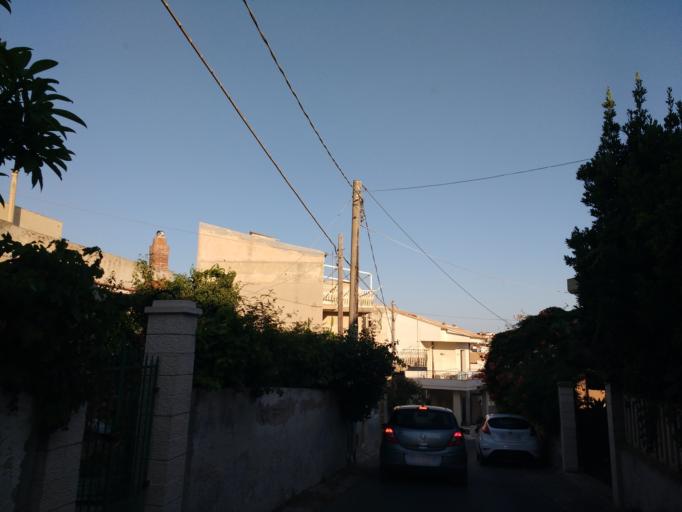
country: IT
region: Sicily
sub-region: Ragusa
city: Cava d'Aliga
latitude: 36.7302
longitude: 14.6833
